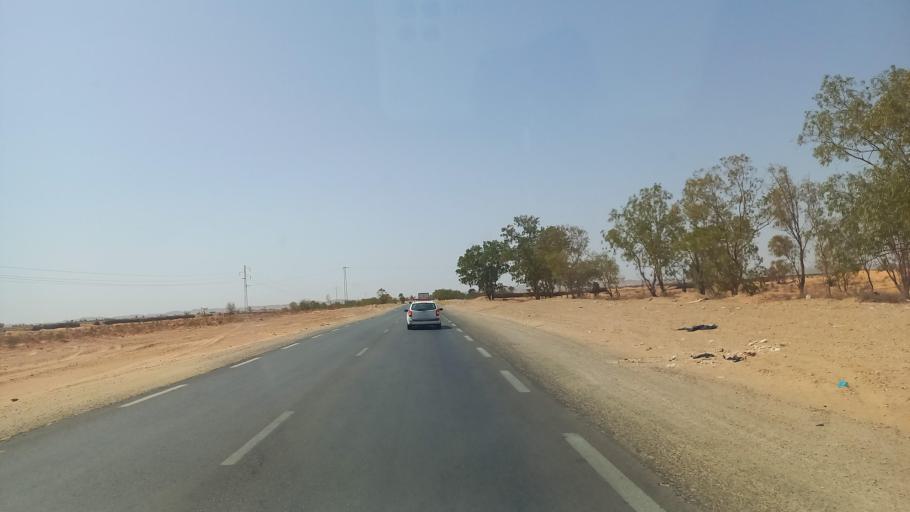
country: TN
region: Madanin
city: Medenine
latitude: 33.2266
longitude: 10.4518
